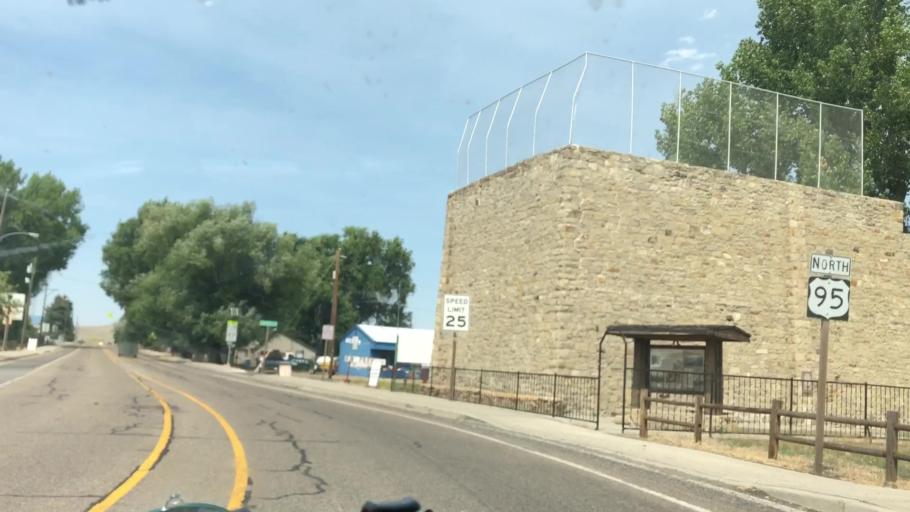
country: US
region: Idaho
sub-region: Owyhee County
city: Murphy
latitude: 42.9742
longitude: -117.0531
